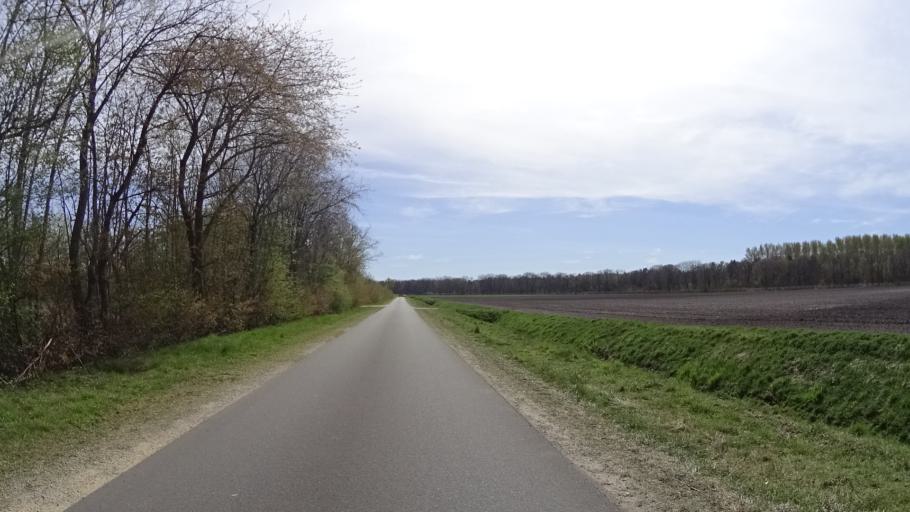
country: DE
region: Lower Saxony
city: Spelle
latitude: 52.3675
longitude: 7.4192
